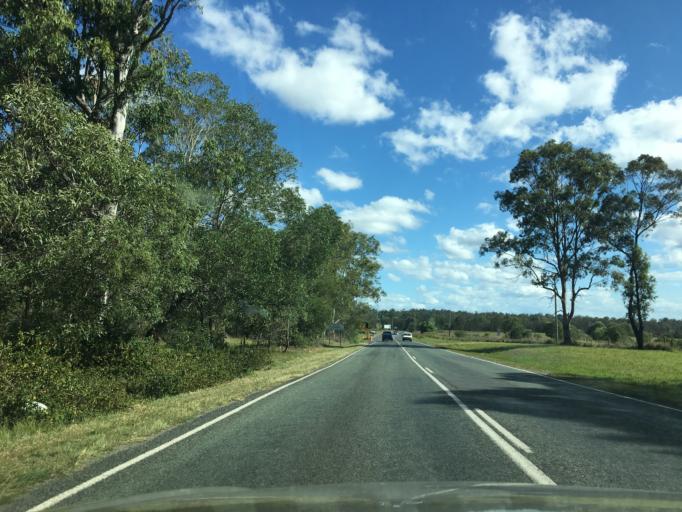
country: AU
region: Queensland
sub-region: Logan
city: Logan Reserve
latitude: -27.7471
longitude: 153.1260
